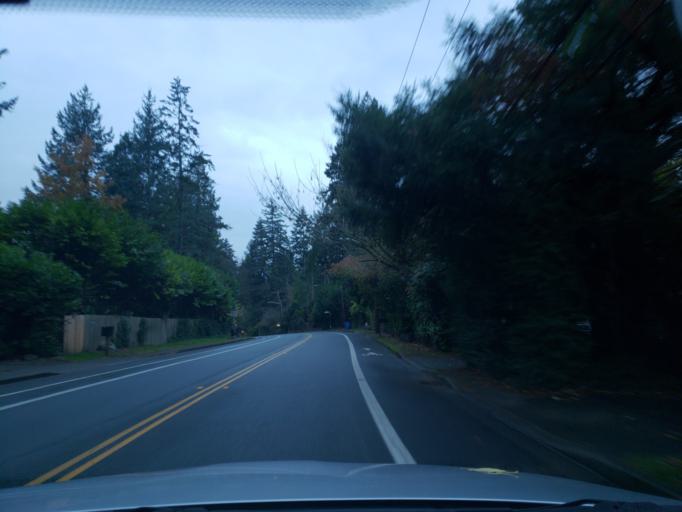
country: US
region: Washington
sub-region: King County
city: Kenmore
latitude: 47.7513
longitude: -122.2397
